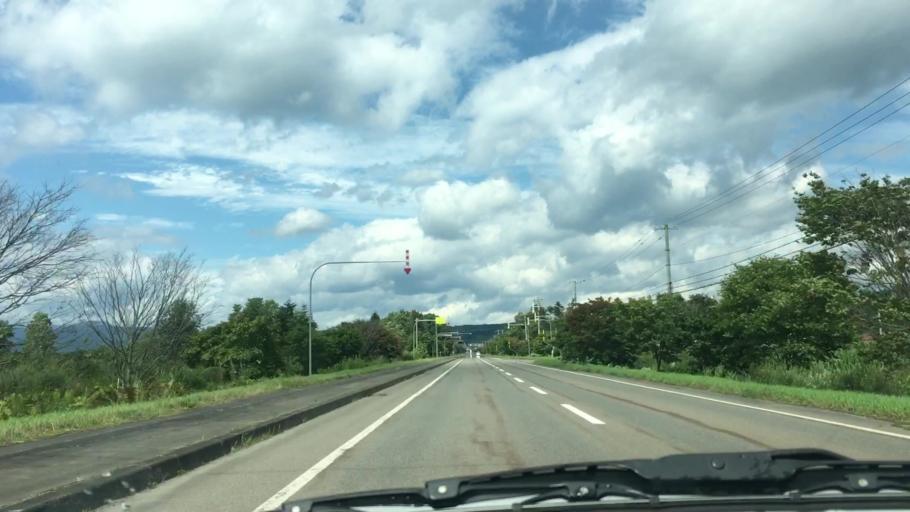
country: JP
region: Hokkaido
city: Otofuke
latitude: 43.2926
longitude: 143.3086
